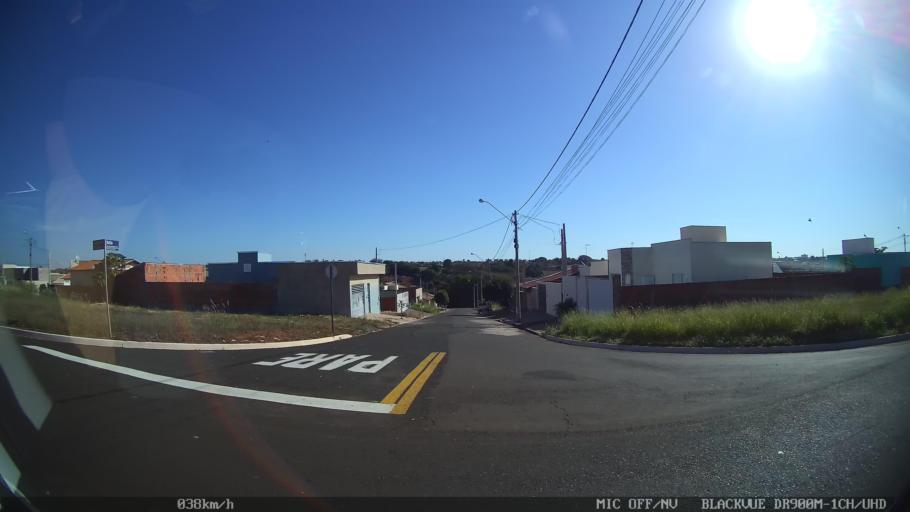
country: BR
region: Sao Paulo
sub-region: Olimpia
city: Olimpia
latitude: -20.7387
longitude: -48.8825
